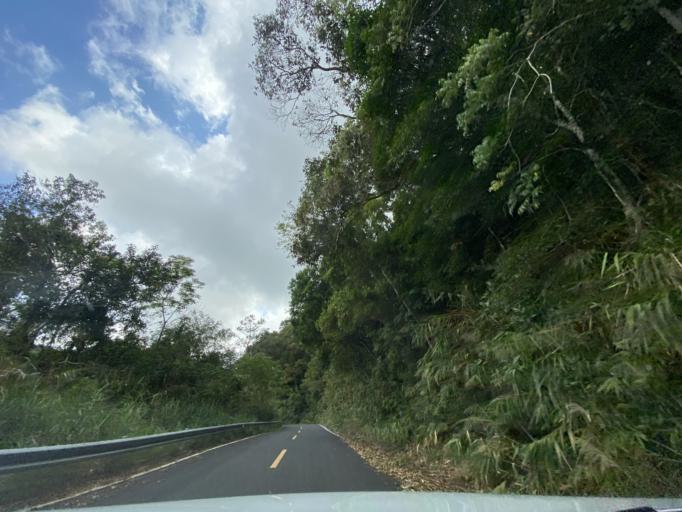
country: CN
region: Hainan
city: Diaoluoshan
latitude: 18.7089
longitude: 109.8828
